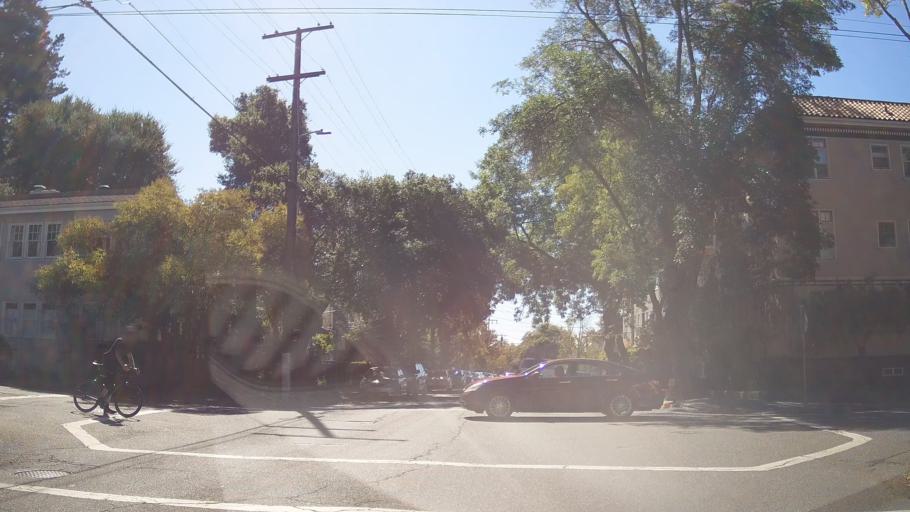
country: US
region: California
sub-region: Alameda County
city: Berkeley
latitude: 37.8541
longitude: -122.2528
